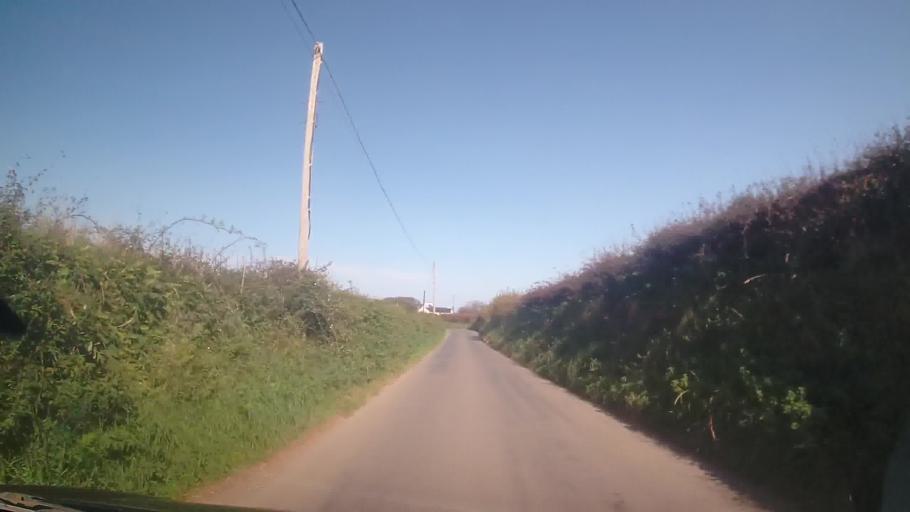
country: GB
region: Wales
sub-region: Pembrokeshire
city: Llanrhian
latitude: 51.9360
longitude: -5.1761
